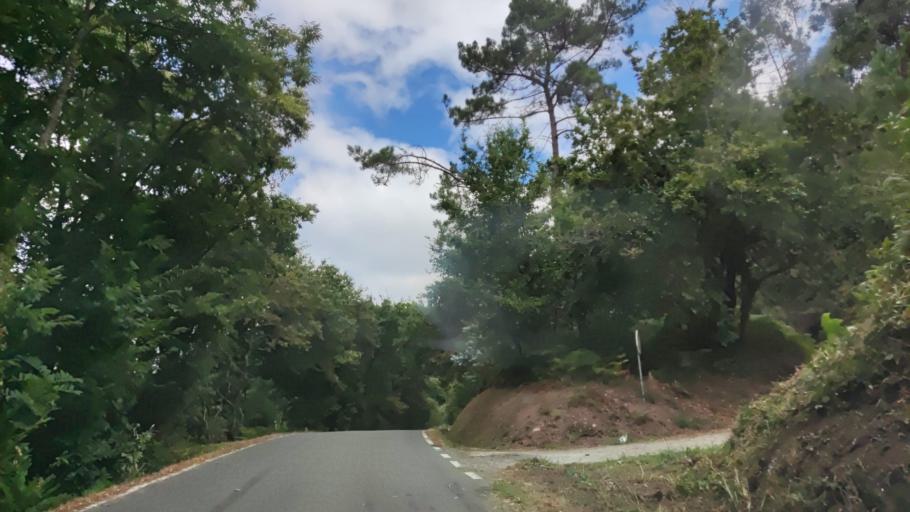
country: ES
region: Galicia
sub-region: Provincia da Coruna
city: Rois
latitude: 42.7451
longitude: -8.6982
